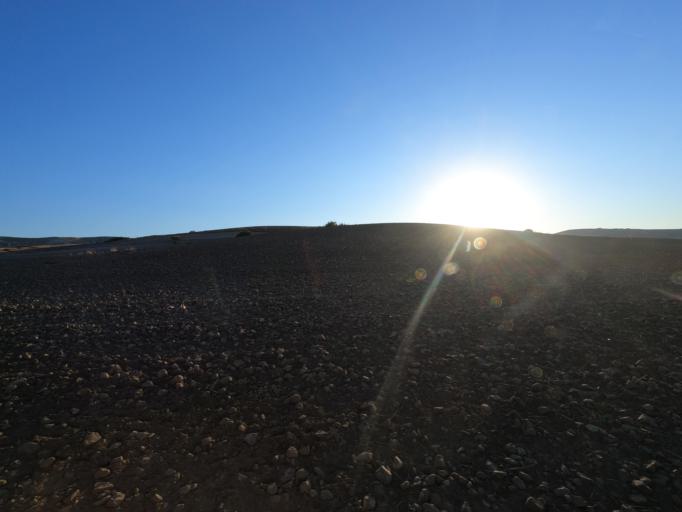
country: CY
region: Larnaka
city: Troulloi
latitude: 35.0258
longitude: 33.6317
